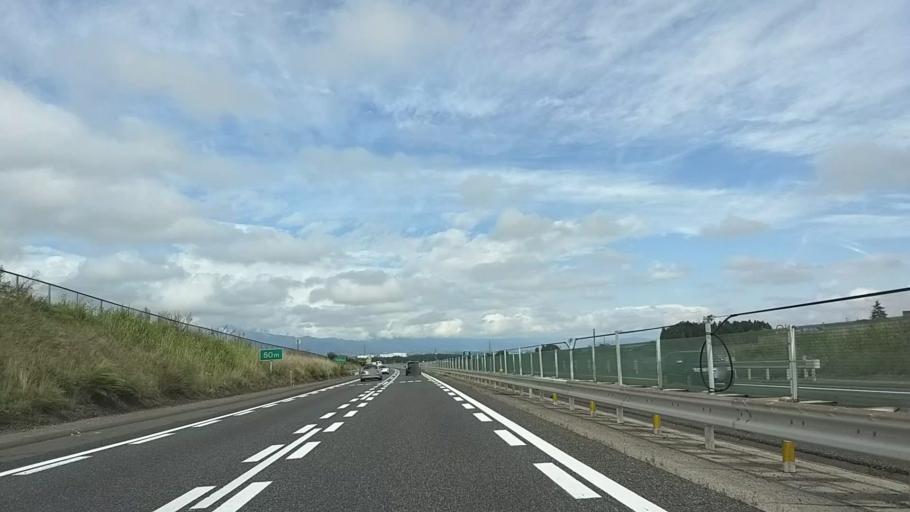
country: JP
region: Nagano
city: Shiojiri
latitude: 36.1268
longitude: 137.9760
